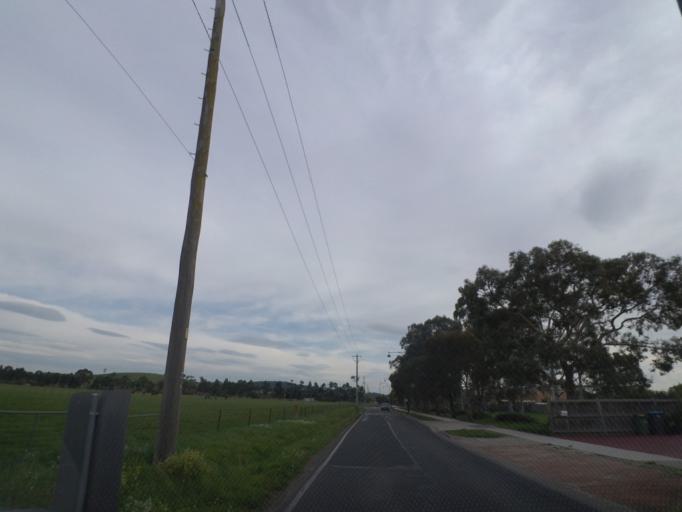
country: AU
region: Victoria
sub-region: Knox
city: Ferntree Gully
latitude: -37.8973
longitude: 145.2822
